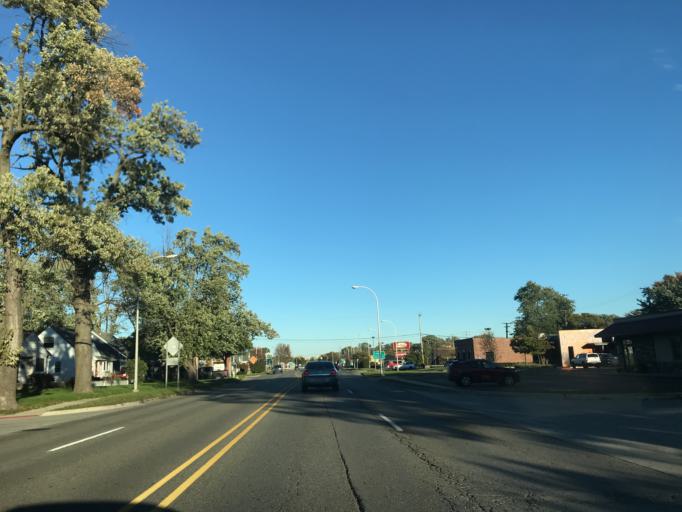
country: US
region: Michigan
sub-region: Oakland County
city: Madison Heights
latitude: 42.4904
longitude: -83.1204
